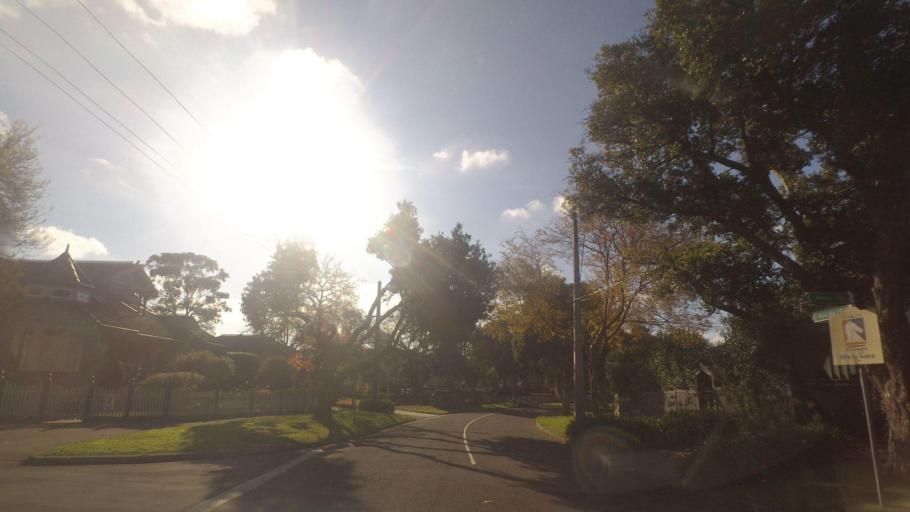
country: AU
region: Victoria
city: Mont Albert
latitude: -37.8101
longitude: 145.1025
